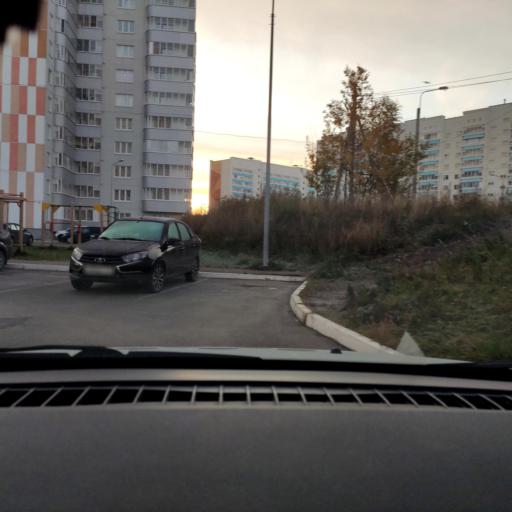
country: RU
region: Perm
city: Perm
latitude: 58.0520
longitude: 56.3471
